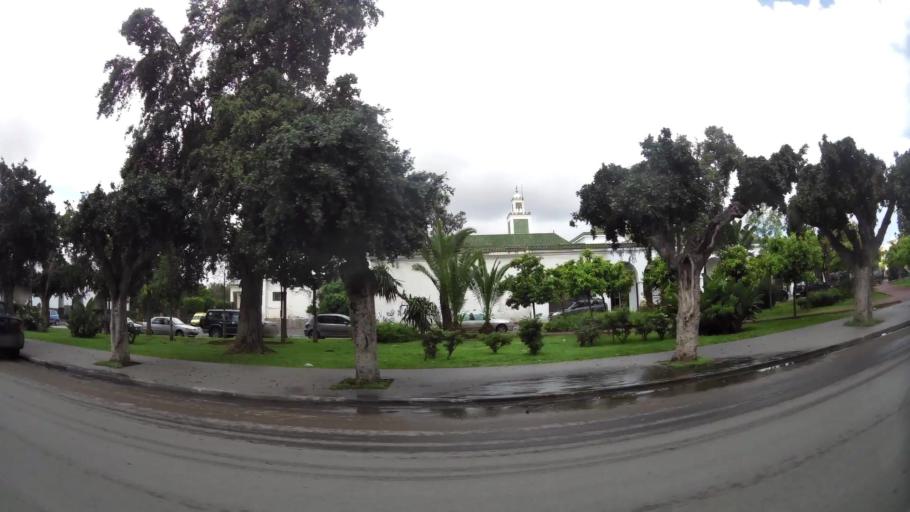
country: MA
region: Grand Casablanca
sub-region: Casablanca
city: Casablanca
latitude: 33.5529
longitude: -7.5987
